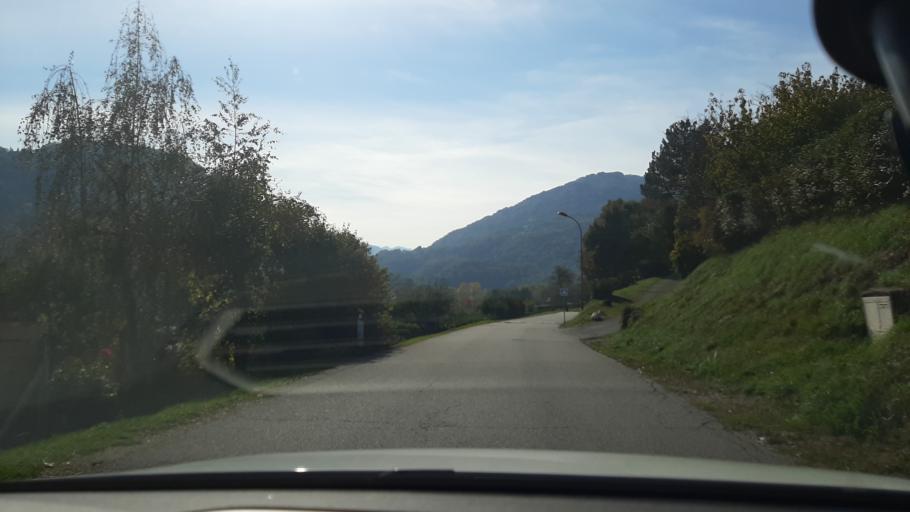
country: FR
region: Rhone-Alpes
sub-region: Departement de la Savoie
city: La Rochette
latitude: 45.4566
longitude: 6.1041
